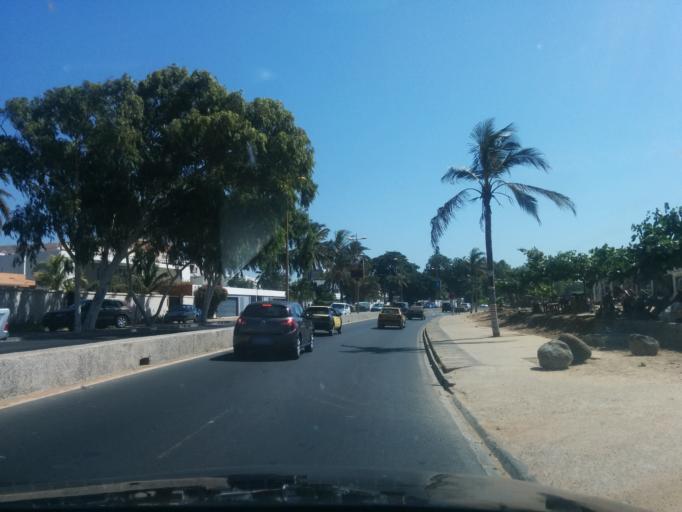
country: SN
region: Dakar
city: Mermoz Boabab
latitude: 14.7003
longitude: -17.4736
